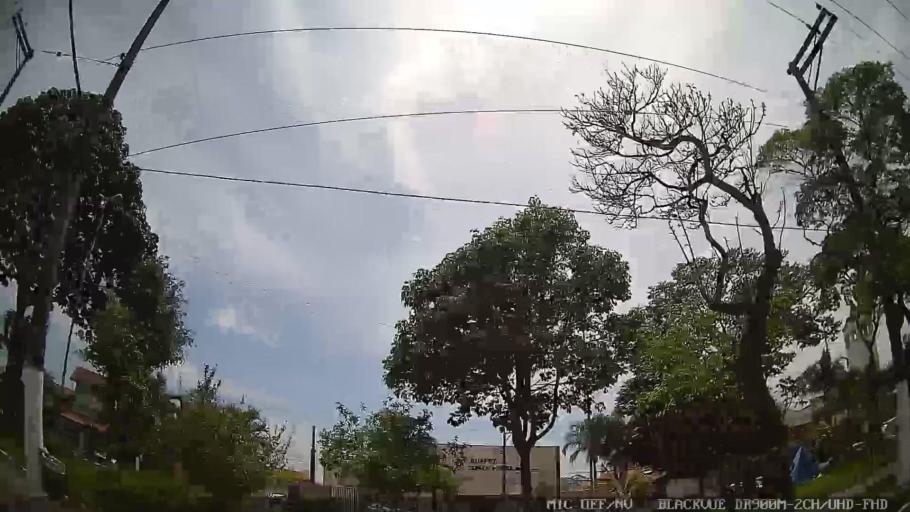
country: BR
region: Sao Paulo
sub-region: Sao Caetano Do Sul
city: Sao Caetano do Sul
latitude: -23.5641
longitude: -46.5485
